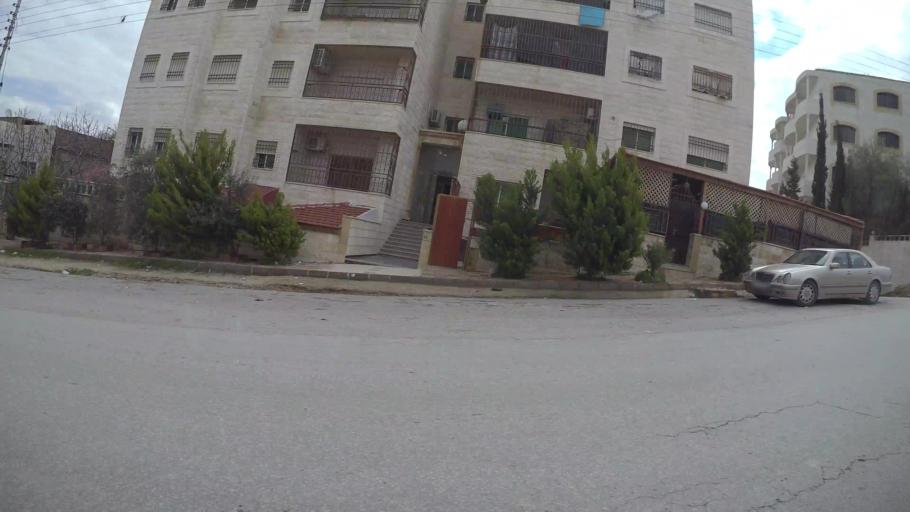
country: JO
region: Amman
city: Al Jubayhah
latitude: 32.0574
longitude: 35.8280
